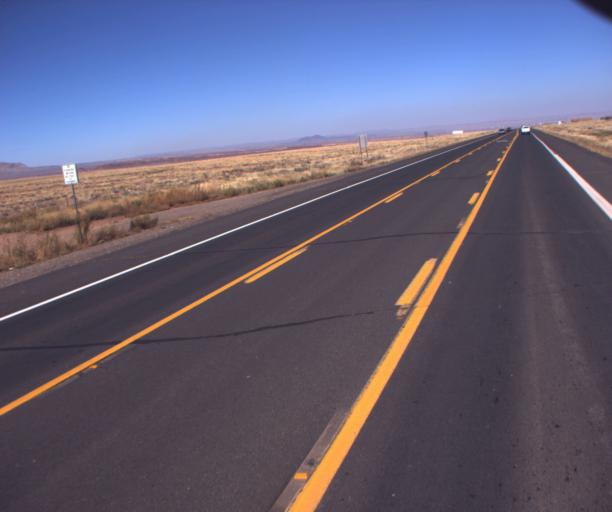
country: US
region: Arizona
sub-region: Coconino County
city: Tuba City
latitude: 35.7467
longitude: -111.4731
